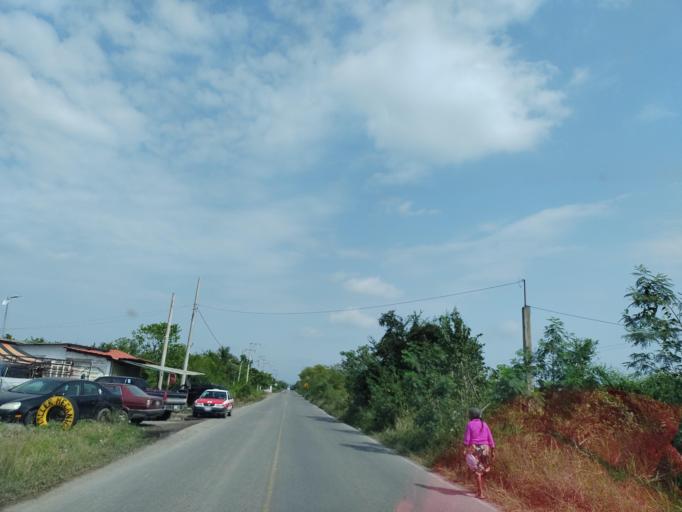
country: MX
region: Puebla
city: Espinal
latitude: 20.2775
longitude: -97.3307
